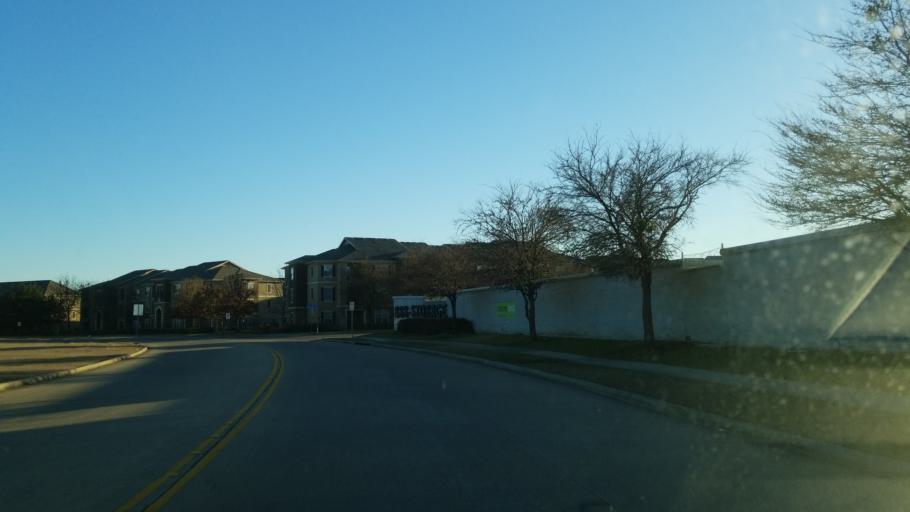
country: US
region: Texas
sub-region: Tarrant County
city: Arlington
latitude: 32.7348
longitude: -97.0597
